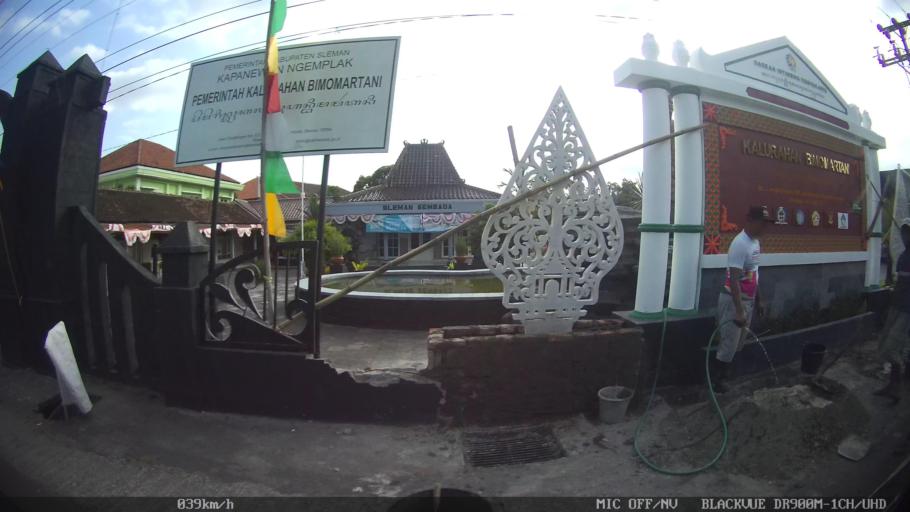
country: ID
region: Central Java
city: Candi Prambanan
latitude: -7.6996
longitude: 110.4655
